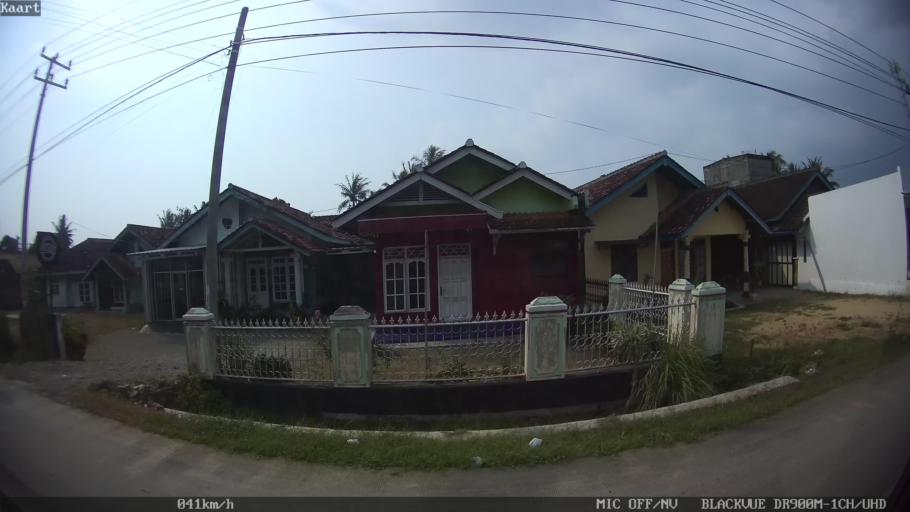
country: ID
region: Lampung
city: Gadingrejo
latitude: -5.3796
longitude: 105.0297
